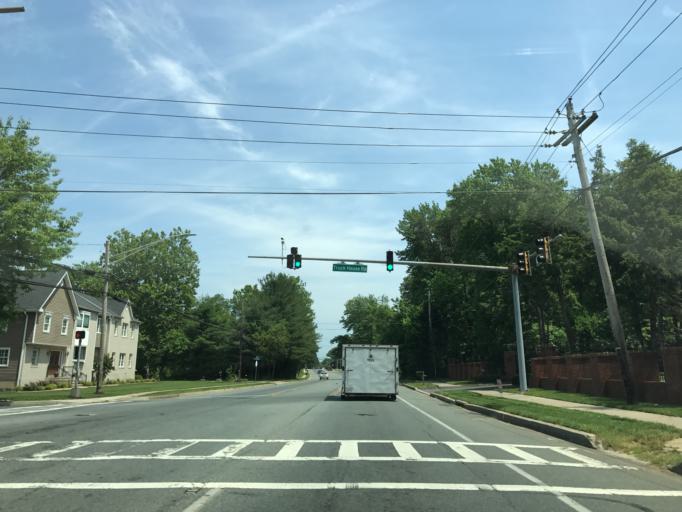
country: US
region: Maryland
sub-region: Anne Arundel County
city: Arden on the Severn
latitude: 39.0785
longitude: -76.5726
